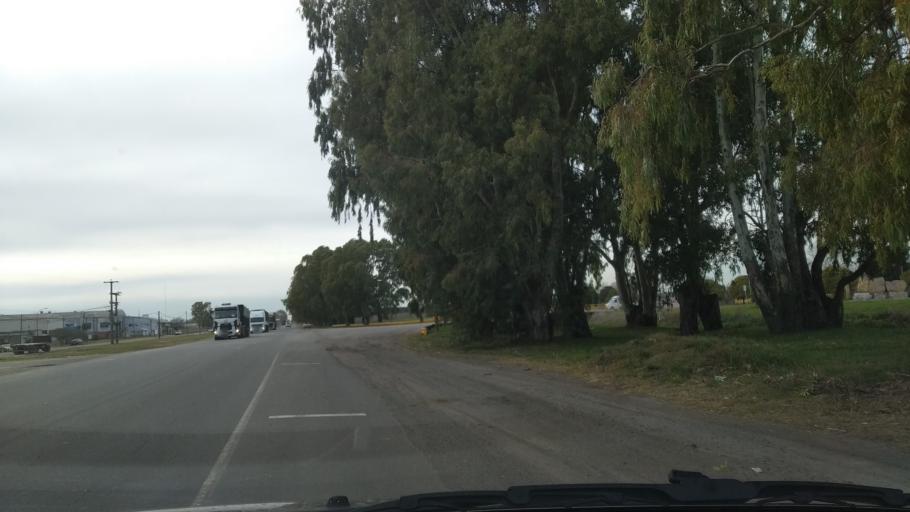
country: AR
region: Buenos Aires
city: Olavarria
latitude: -36.9762
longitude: -60.2801
